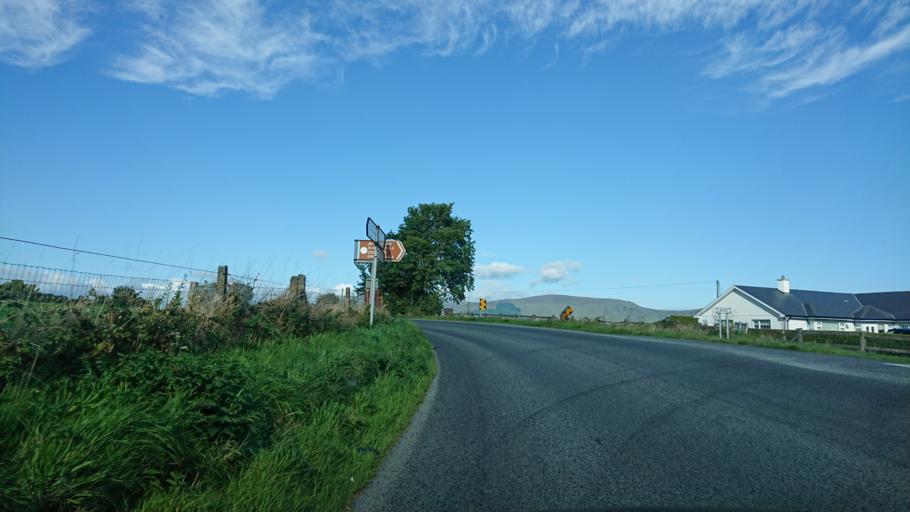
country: IE
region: Munster
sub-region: Waterford
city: Dungarvan
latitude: 52.1578
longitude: -7.6886
